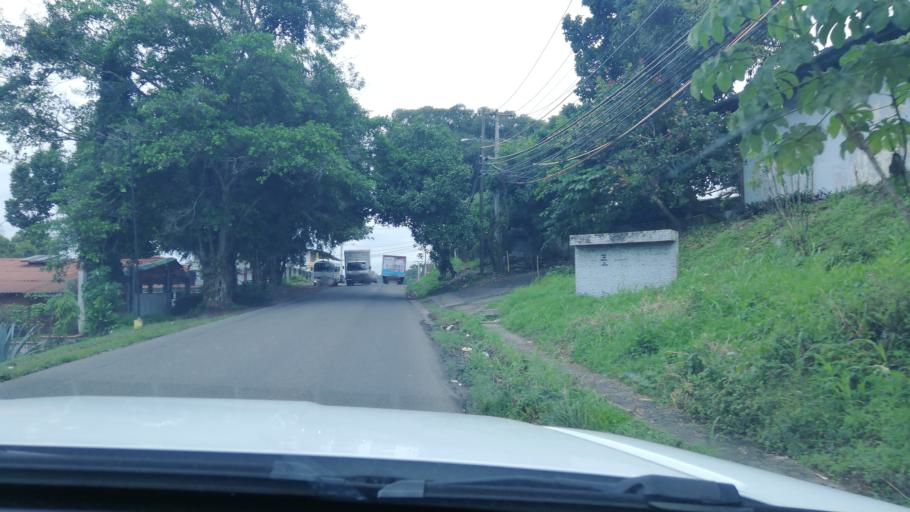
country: PA
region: Panama
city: Las Cumbres
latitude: 9.0770
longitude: -79.5241
